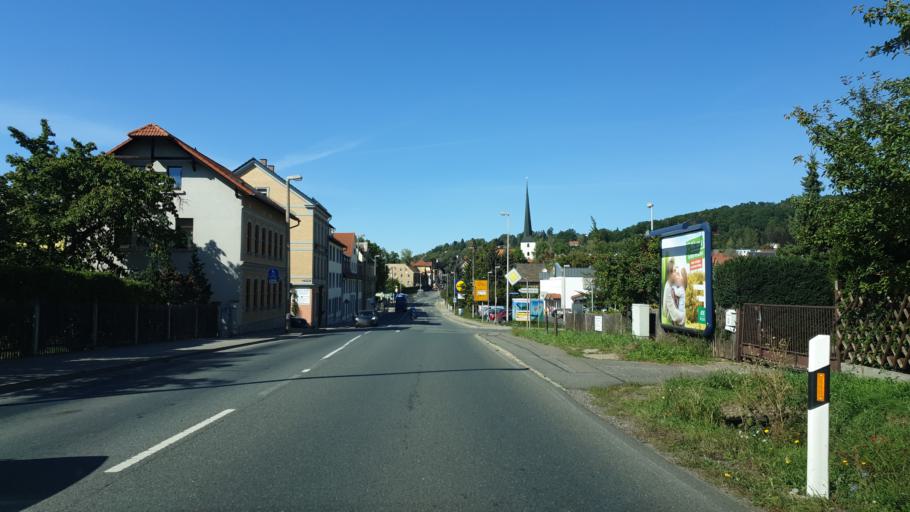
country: DE
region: Thuringia
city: Gera
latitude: 50.9175
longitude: 12.0554
